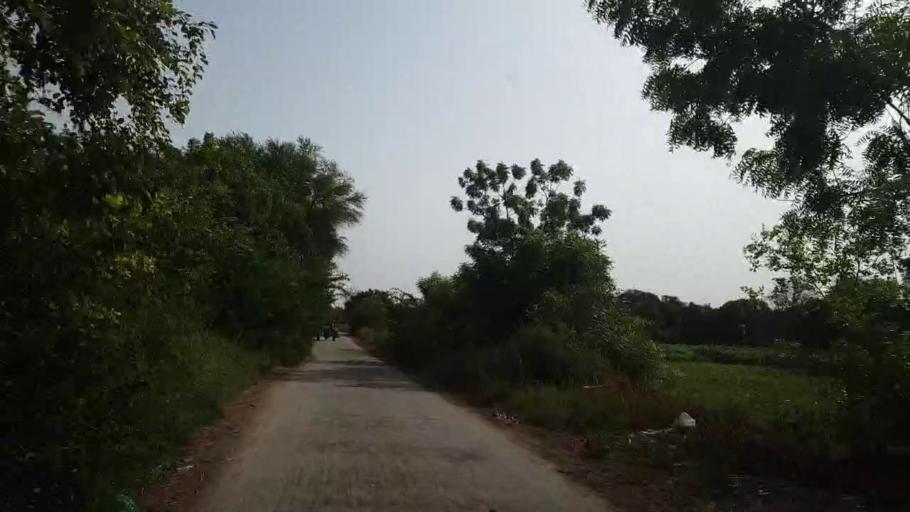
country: PK
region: Sindh
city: Nawabshah
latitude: 26.2303
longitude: 68.4069
